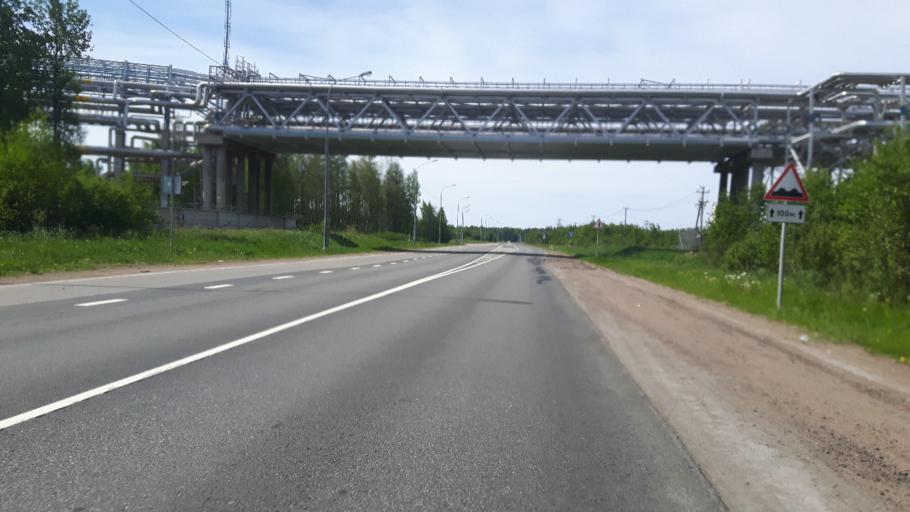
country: RU
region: Leningrad
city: Ust'-Luga
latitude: 59.6553
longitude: 28.3836
